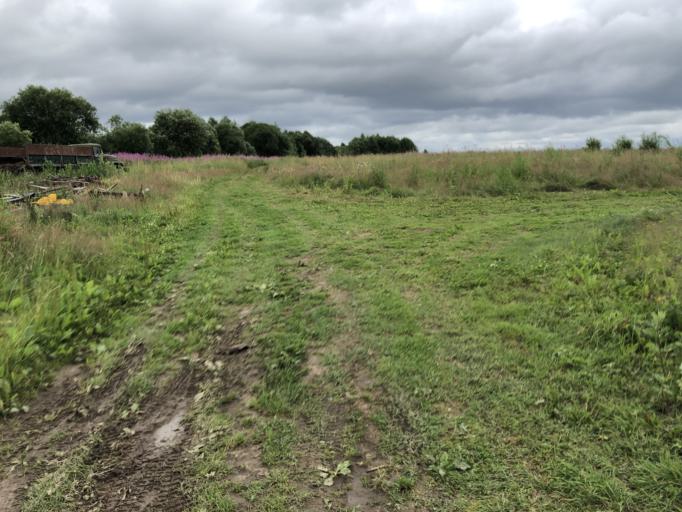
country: RU
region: Tverskaya
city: Rzhev
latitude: 56.2397
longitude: 34.3803
